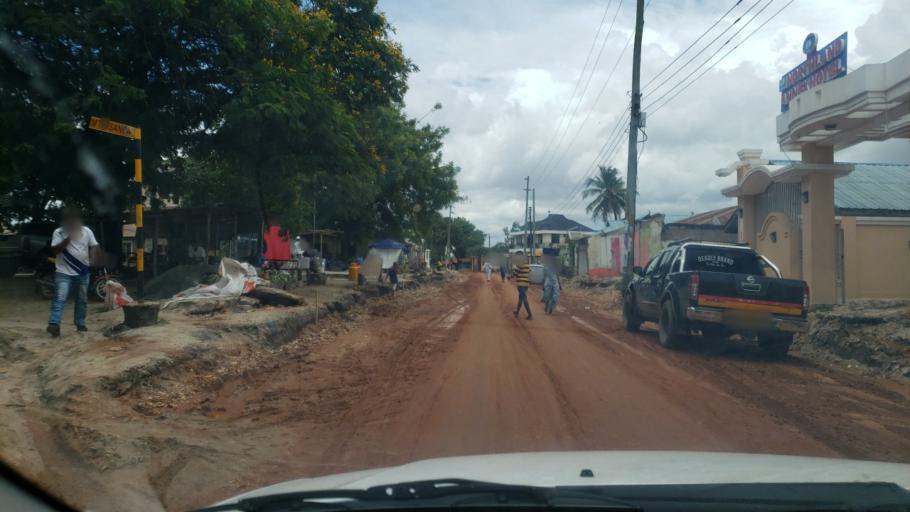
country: TZ
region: Dar es Salaam
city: Magomeni
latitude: -6.8090
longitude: 39.2521
